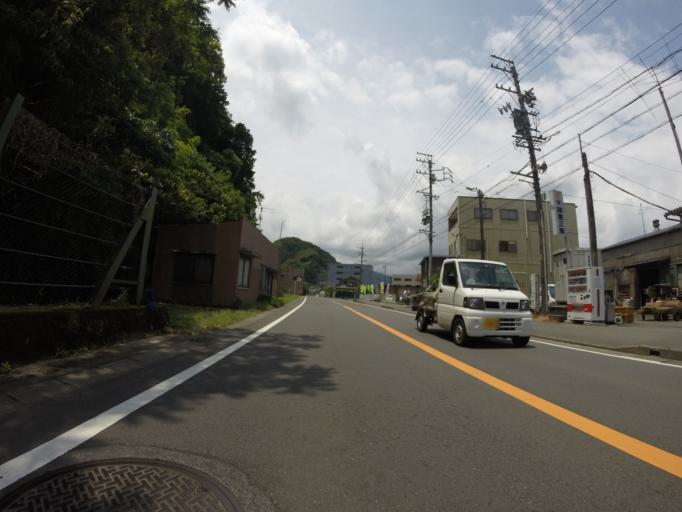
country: JP
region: Shizuoka
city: Shizuoka-shi
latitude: 34.9774
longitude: 138.3355
